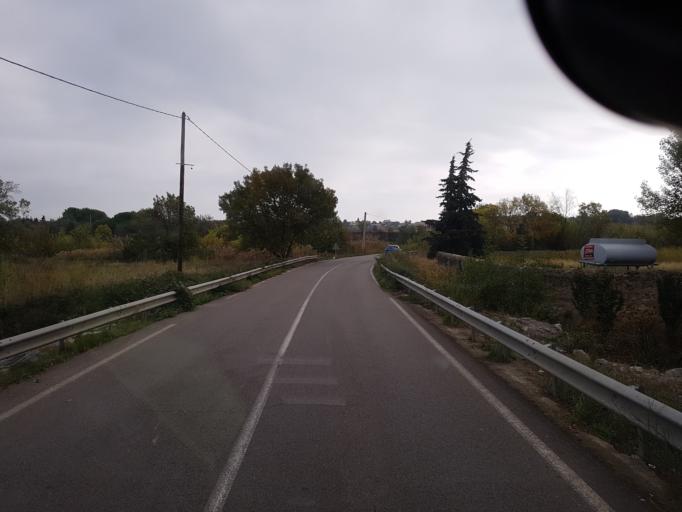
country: FR
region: Languedoc-Roussillon
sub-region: Departement de l'Herault
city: Loupian
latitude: 43.4496
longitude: 3.5992
